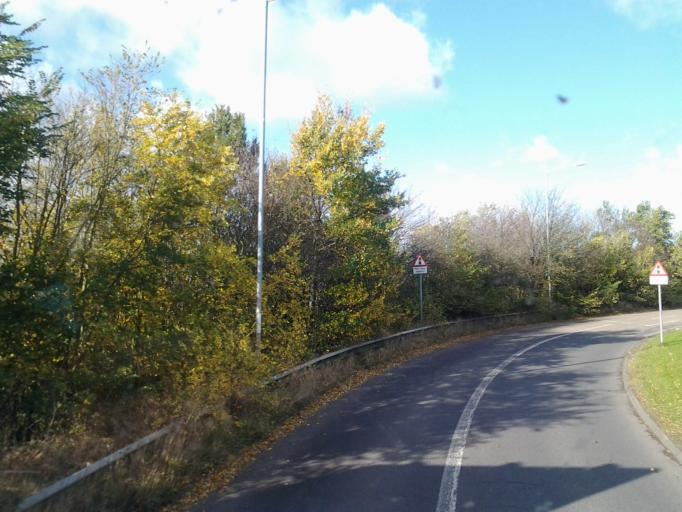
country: GB
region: England
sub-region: Gateshead
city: Lamesley
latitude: 54.9098
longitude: -1.5844
